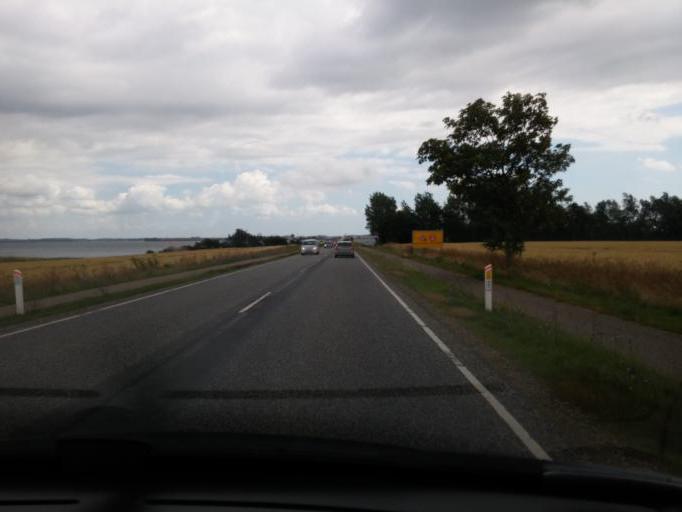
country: DK
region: South Denmark
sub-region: Langeland Kommune
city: Rudkobing
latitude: 54.9703
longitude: 10.6472
